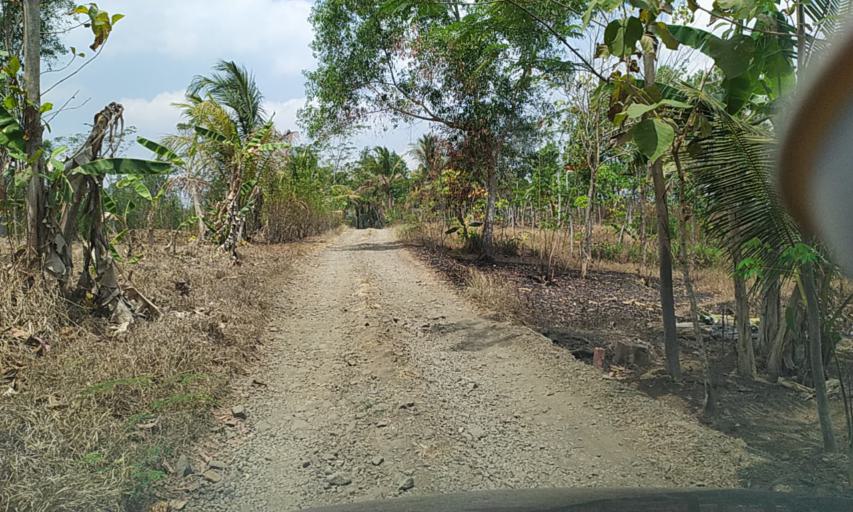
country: ID
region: Central Java
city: Kemantren Satu
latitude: -7.5259
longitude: 108.9222
